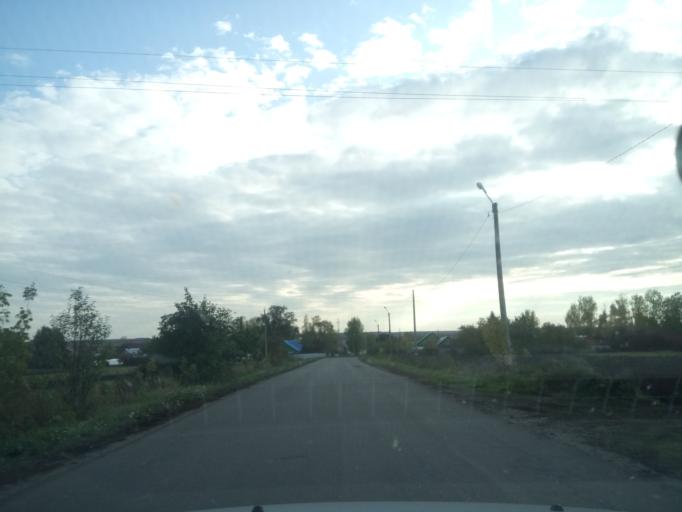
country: RU
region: Nizjnij Novgorod
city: Bol'shoye Boldino
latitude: 54.9974
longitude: 45.3157
